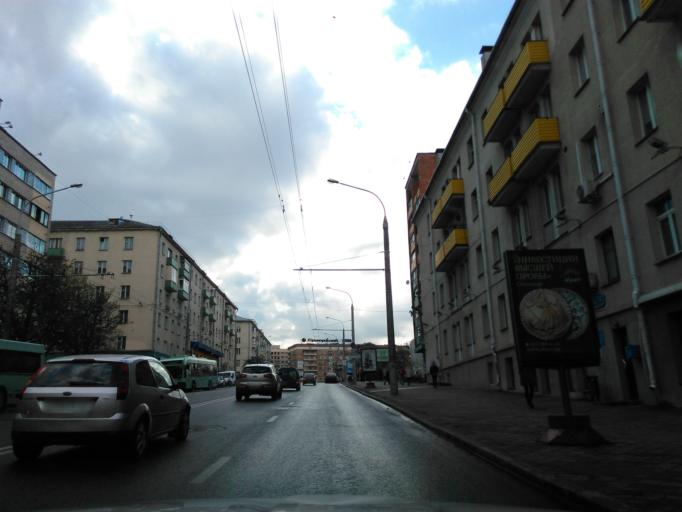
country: BY
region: Minsk
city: Minsk
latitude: 53.9039
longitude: 27.5443
